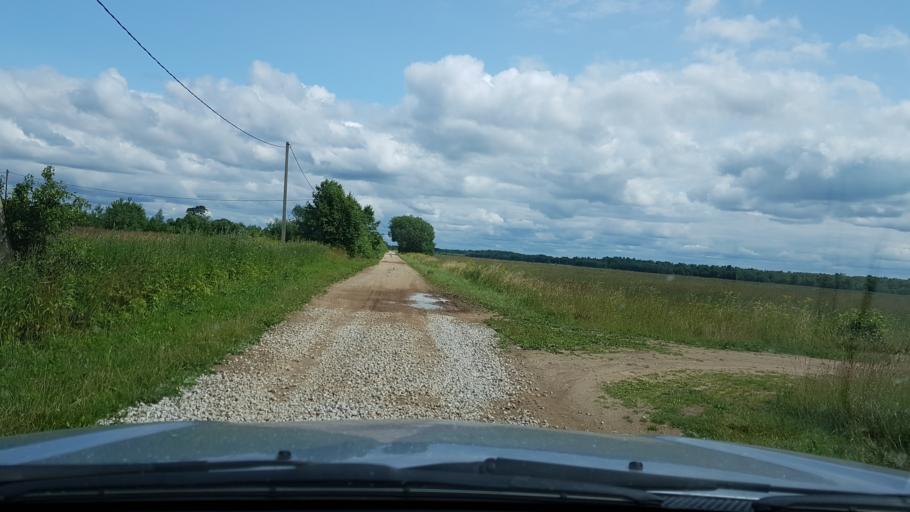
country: EE
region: Ida-Virumaa
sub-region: Sillamaee linn
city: Sillamae
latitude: 59.3678
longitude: 27.8531
